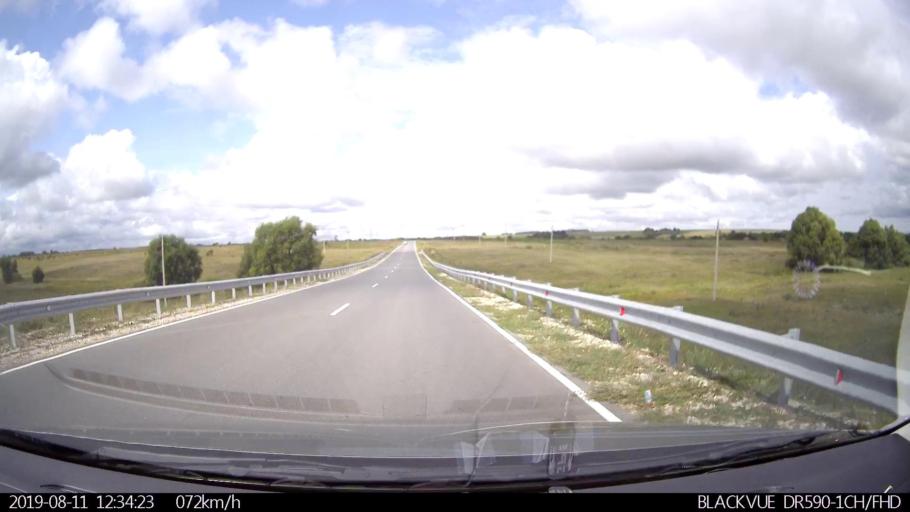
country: RU
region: Ulyanovsk
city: Ignatovka
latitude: 53.8165
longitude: 47.8435
